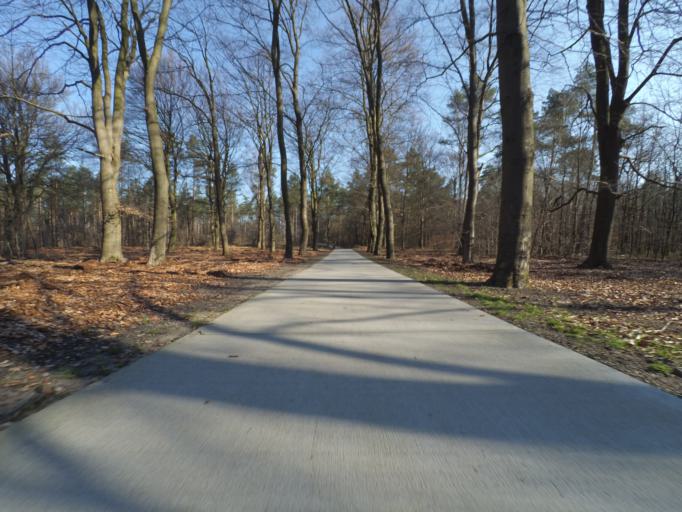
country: NL
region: Gelderland
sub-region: Gemeente Ede
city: Otterlo
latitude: 52.1101
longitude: 5.8706
